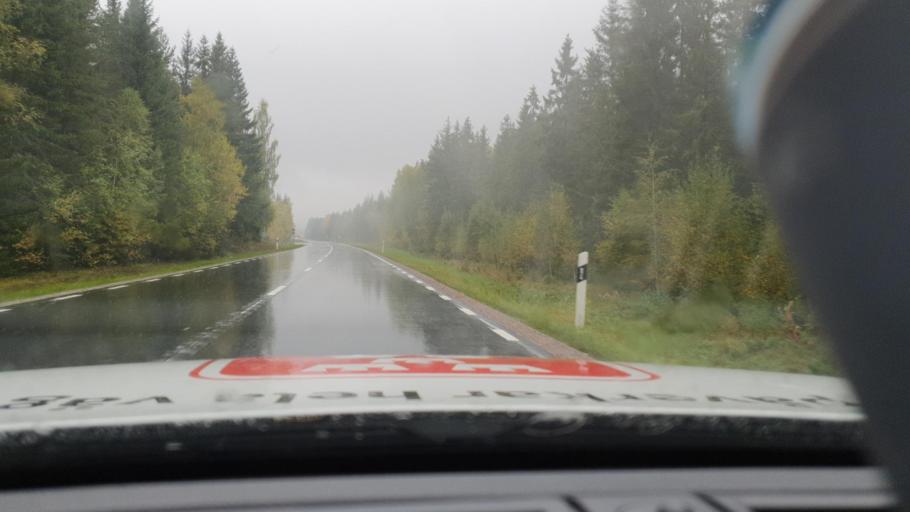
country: SE
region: Uppsala
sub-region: Tierps Kommun
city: Orbyhus
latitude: 60.2718
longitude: 17.6045
